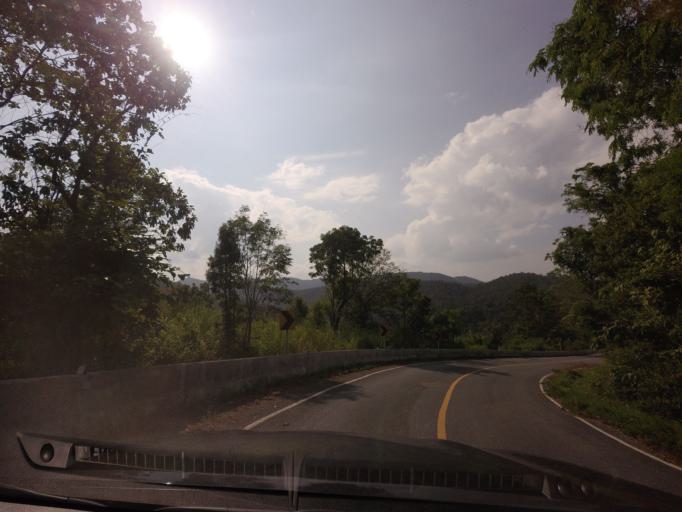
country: TH
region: Uttaradit
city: Ban Khok
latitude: 18.2551
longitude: 100.9934
